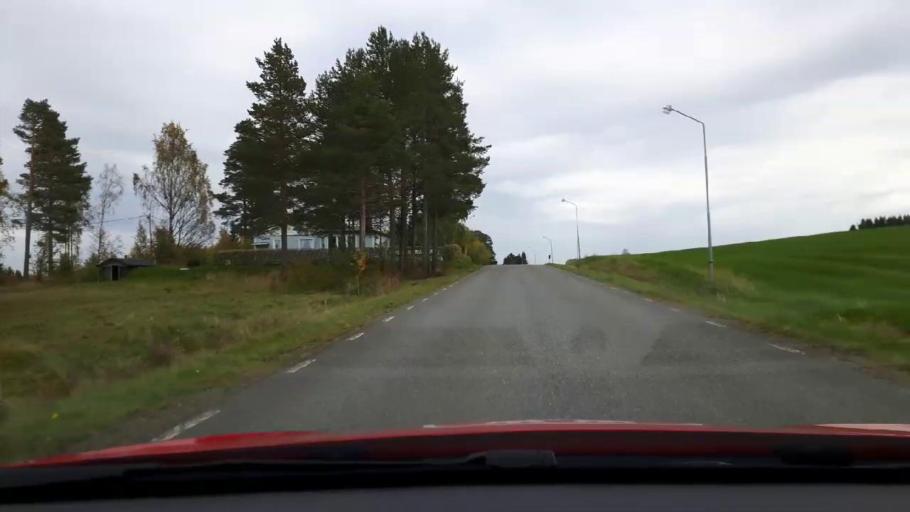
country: SE
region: Jaemtland
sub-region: Krokoms Kommun
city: Krokom
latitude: 63.2289
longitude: 14.1294
